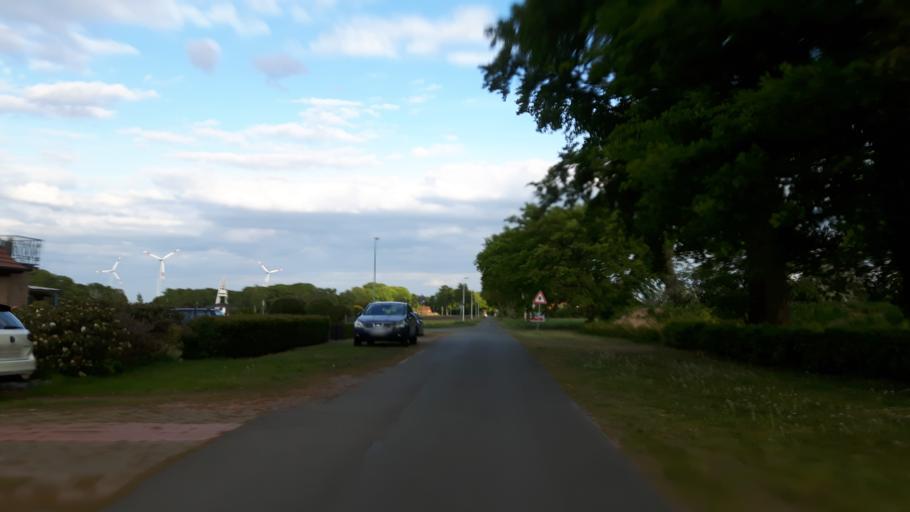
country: DE
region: Lower Saxony
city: Gross Ippener
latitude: 53.0117
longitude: 8.5993
